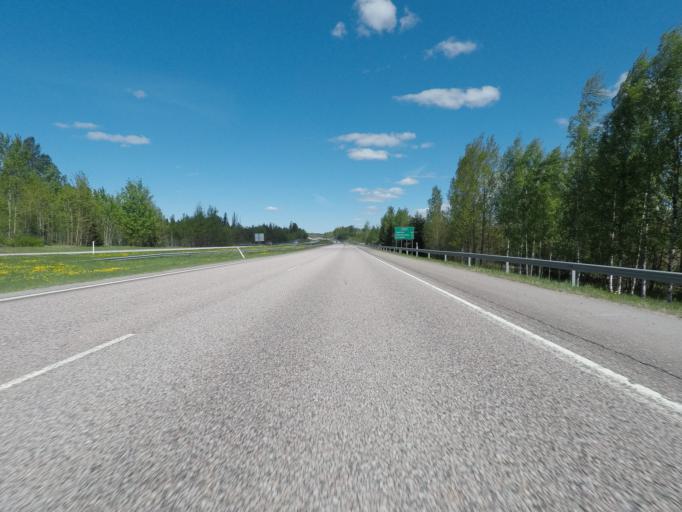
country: FI
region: Uusimaa
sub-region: Helsinki
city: Nurmijaervi
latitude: 60.4656
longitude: 24.8499
